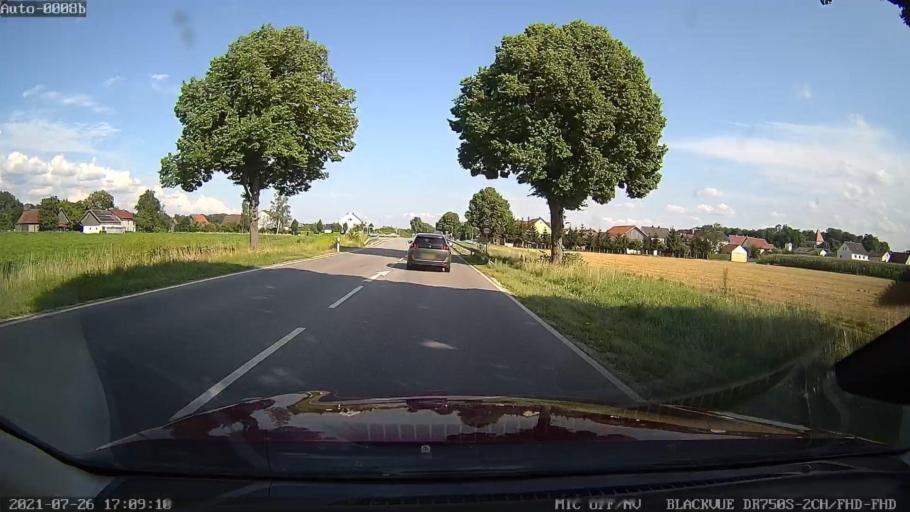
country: DE
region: Bavaria
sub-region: Upper Palatinate
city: Mintraching
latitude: 48.9863
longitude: 12.2526
